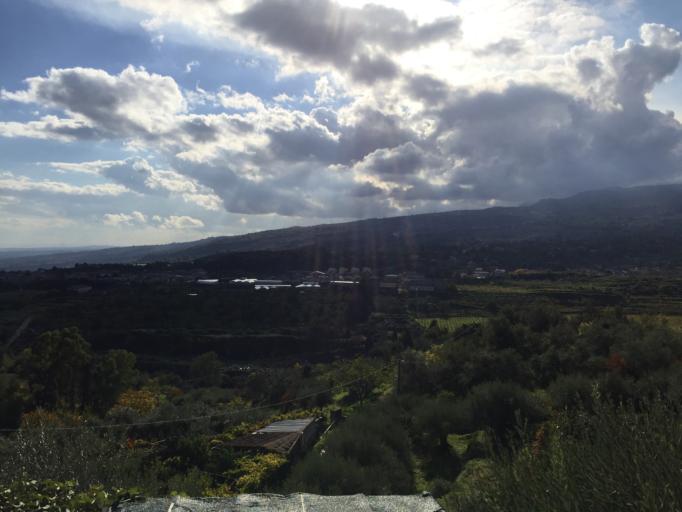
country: IT
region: Sicily
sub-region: Catania
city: Piedimonte Etneo
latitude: 37.8185
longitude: 15.1779
